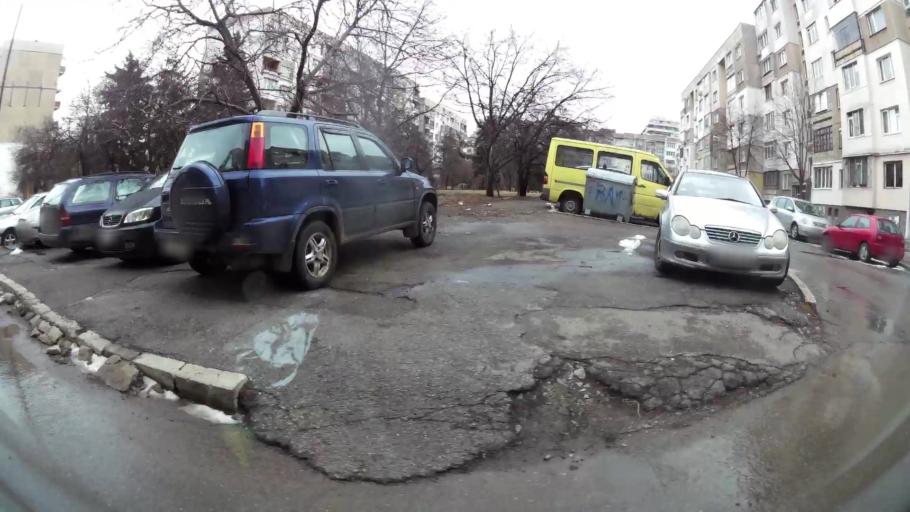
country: BG
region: Sofiya
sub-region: Obshtina Bozhurishte
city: Bozhurishte
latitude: 42.7257
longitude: 23.2469
